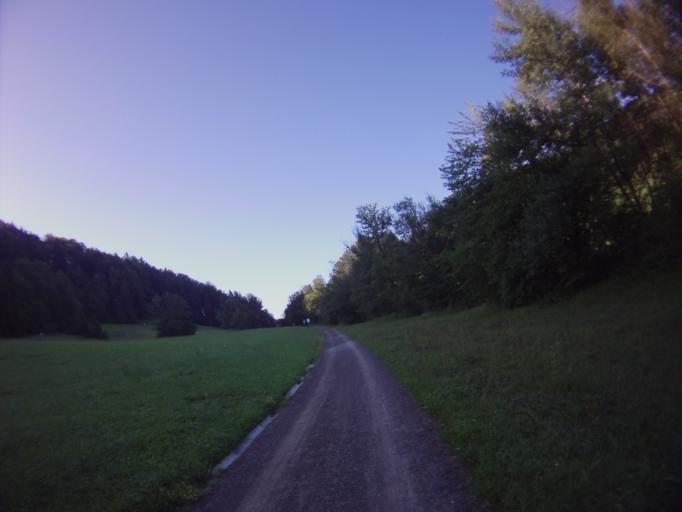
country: CH
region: Zug
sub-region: Zug
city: Unterageri
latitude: 47.1590
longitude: 8.5606
